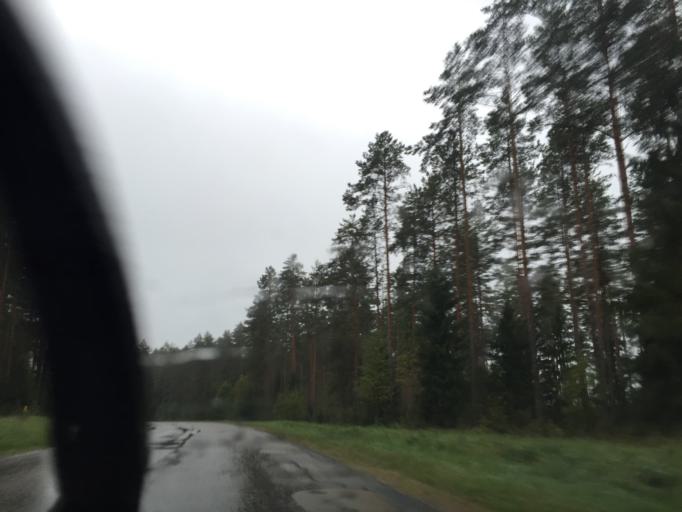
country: LV
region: Incukalns
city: Incukalns
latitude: 57.0419
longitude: 24.6773
